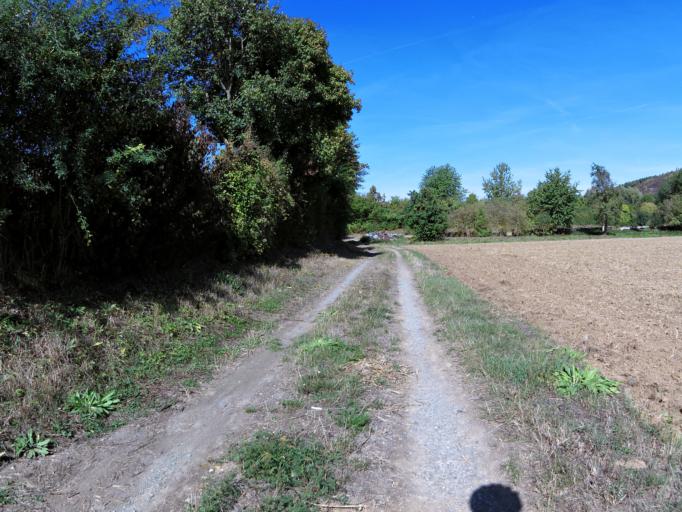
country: DE
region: Bavaria
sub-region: Regierungsbezirk Unterfranken
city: Margetshochheim
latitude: 49.8484
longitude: 9.8567
